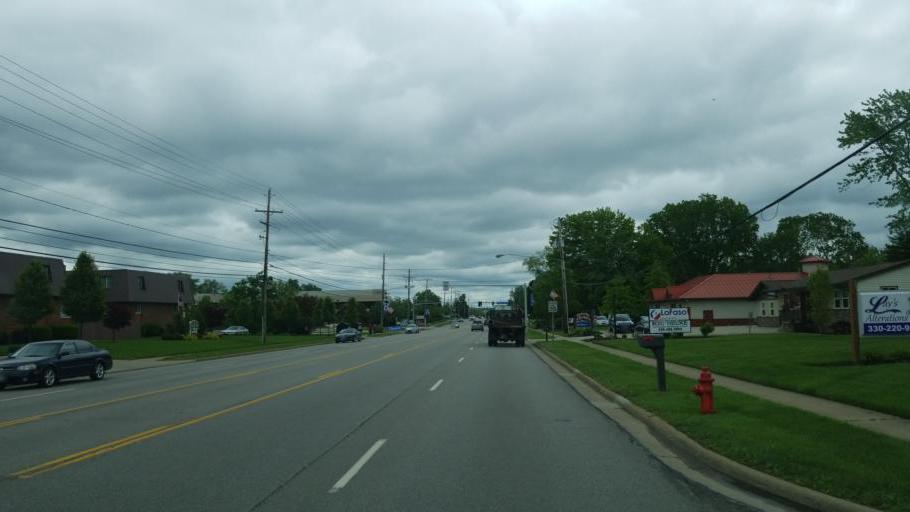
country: US
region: Ohio
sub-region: Medina County
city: Brunswick
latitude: 41.2382
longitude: -81.8348
